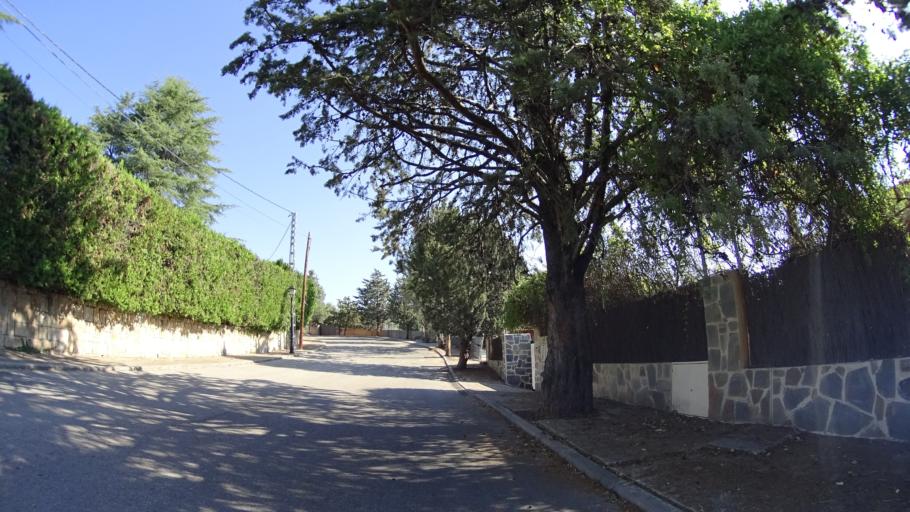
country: ES
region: Madrid
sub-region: Provincia de Madrid
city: Las Matas
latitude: 40.5751
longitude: -3.9010
